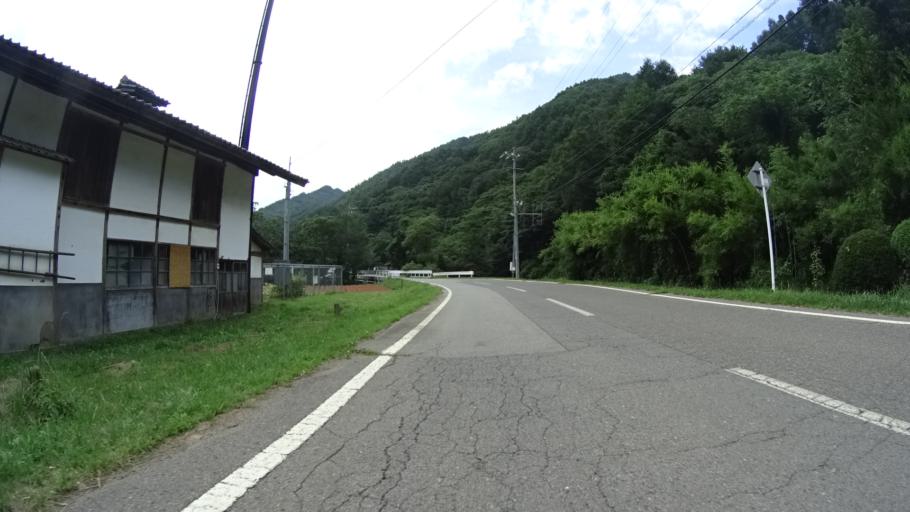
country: JP
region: Nagano
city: Saku
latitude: 36.0665
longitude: 138.5906
